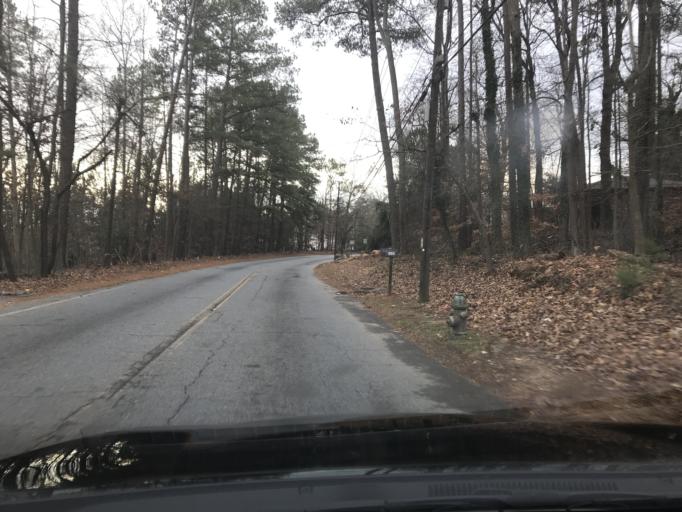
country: US
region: Georgia
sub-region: Fulton County
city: East Point
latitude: 33.7139
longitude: -84.5067
